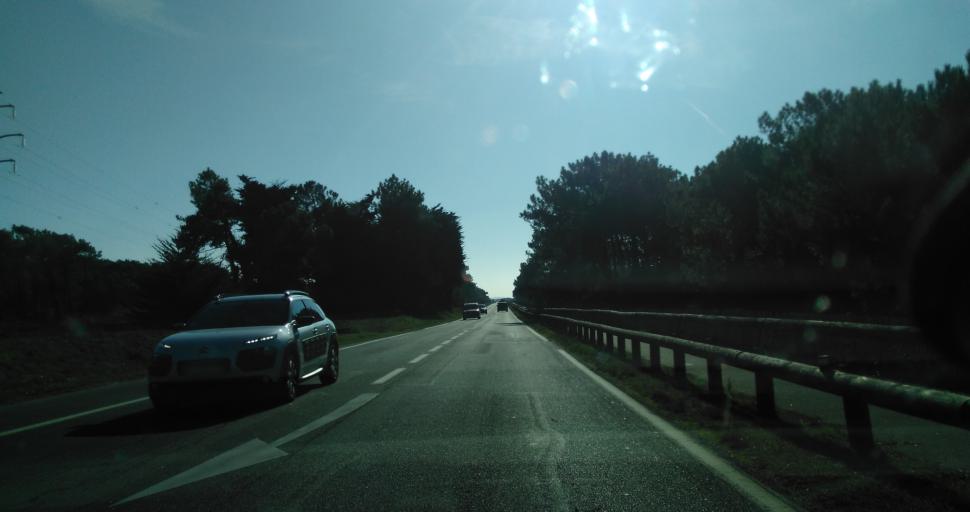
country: FR
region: Brittany
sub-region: Departement du Morbihan
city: Plouharnel
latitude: 47.5925
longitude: -3.1322
